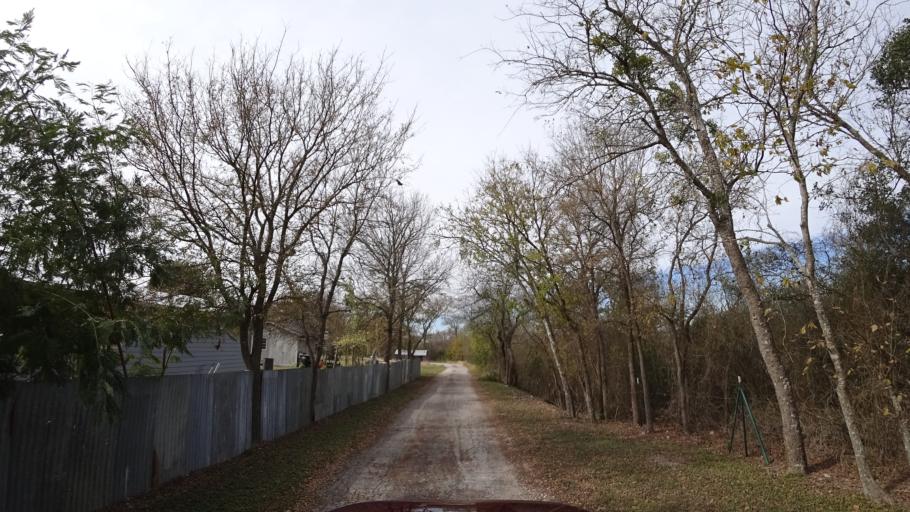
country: US
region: Texas
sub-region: Travis County
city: Garfield
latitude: 30.1464
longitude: -97.5811
